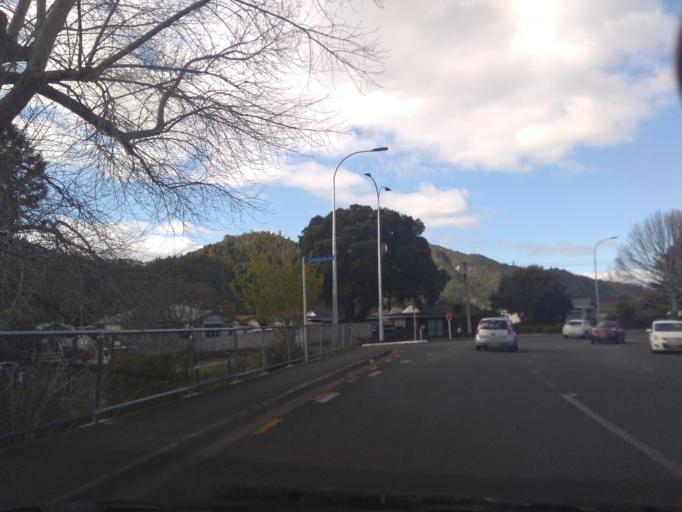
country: NZ
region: Northland
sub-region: Whangarei
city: Whangarei
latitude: -35.7030
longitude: 174.3266
